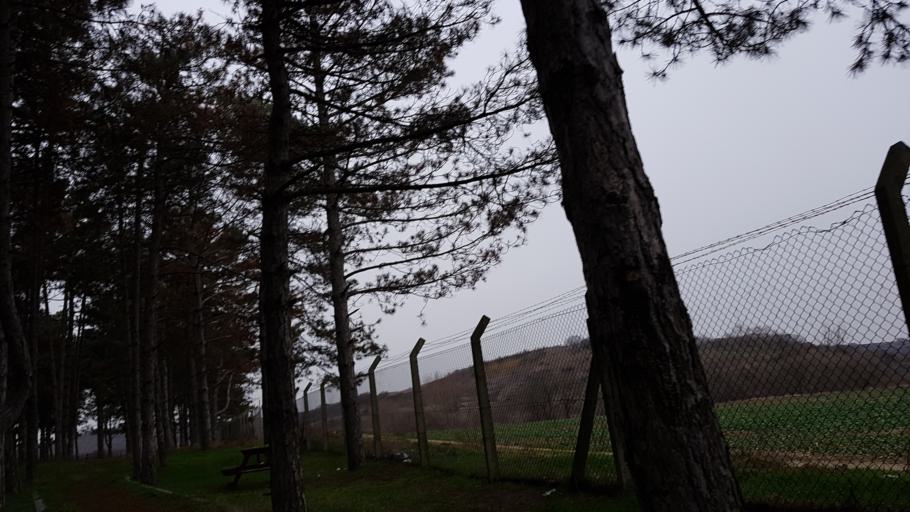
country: TR
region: Tekirdag
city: Muratli
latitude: 41.1851
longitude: 27.4777
